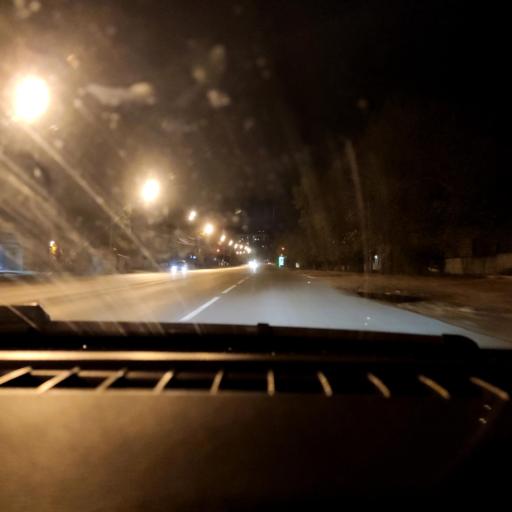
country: RU
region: Voronezj
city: Voronezh
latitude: 51.6558
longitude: 39.2739
